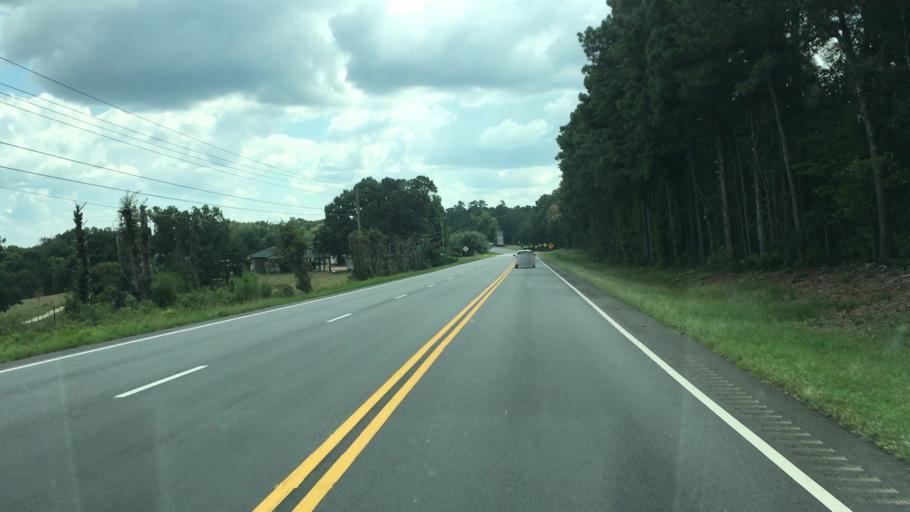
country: US
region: Georgia
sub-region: Putnam County
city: Jefferson
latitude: 33.4225
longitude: -83.3706
